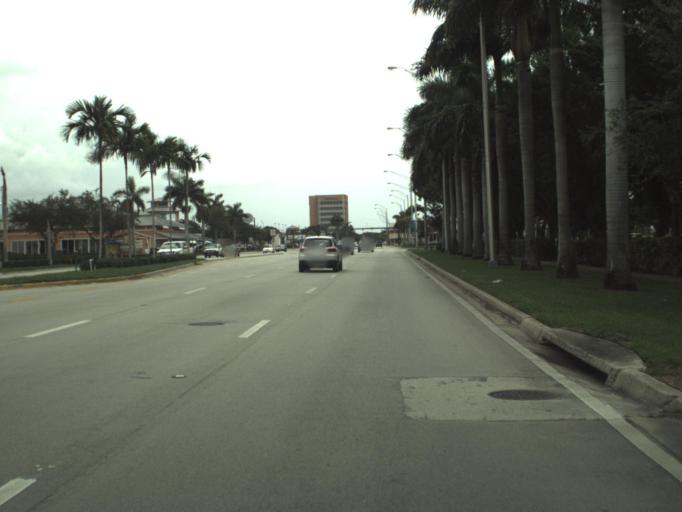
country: US
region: Florida
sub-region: Broward County
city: Terra Mar
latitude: 26.2270
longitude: -80.1025
